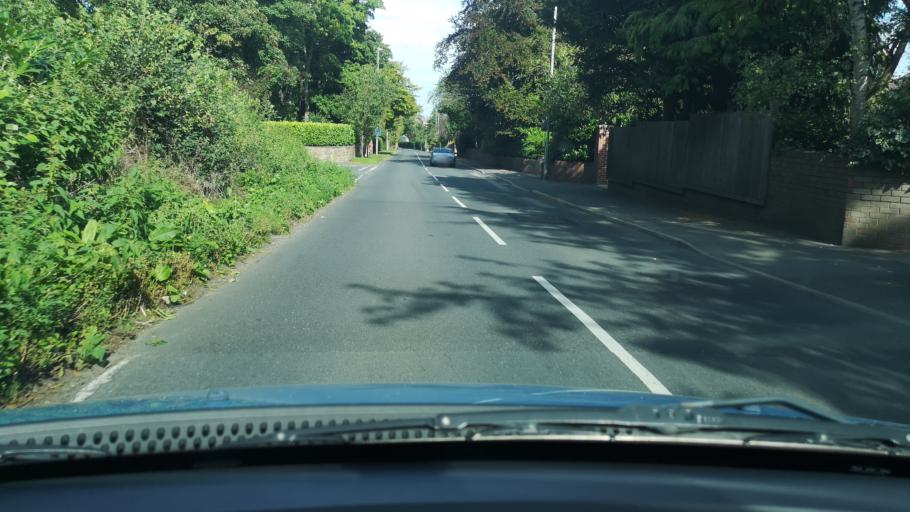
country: GB
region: England
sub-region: City and Borough of Wakefield
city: Walton
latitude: 53.6484
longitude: -1.4805
